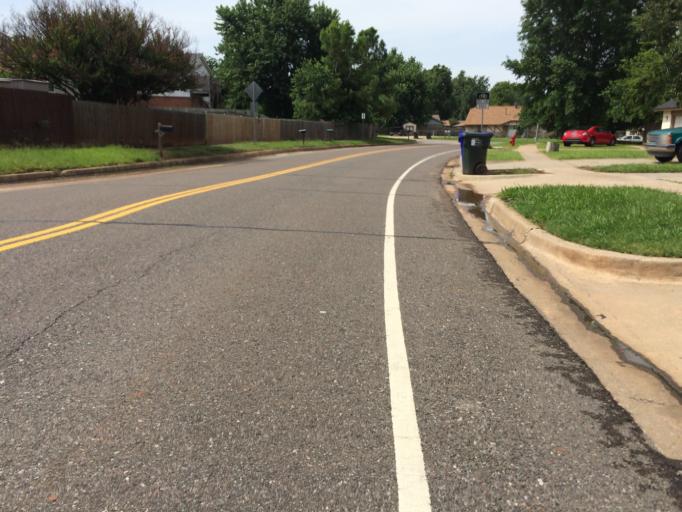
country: US
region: Oklahoma
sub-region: Cleveland County
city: Norman
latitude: 35.1949
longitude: -97.4109
